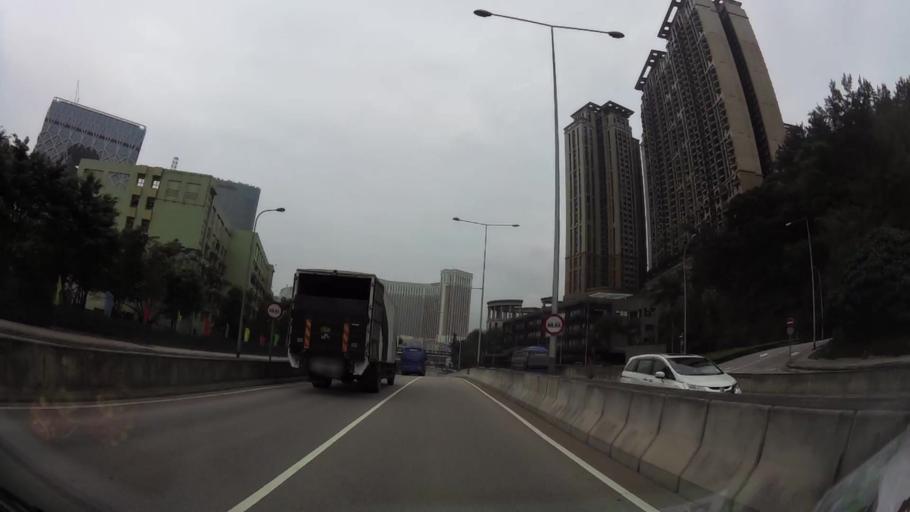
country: MO
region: Macau
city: Macau
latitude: 22.1533
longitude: 113.5661
